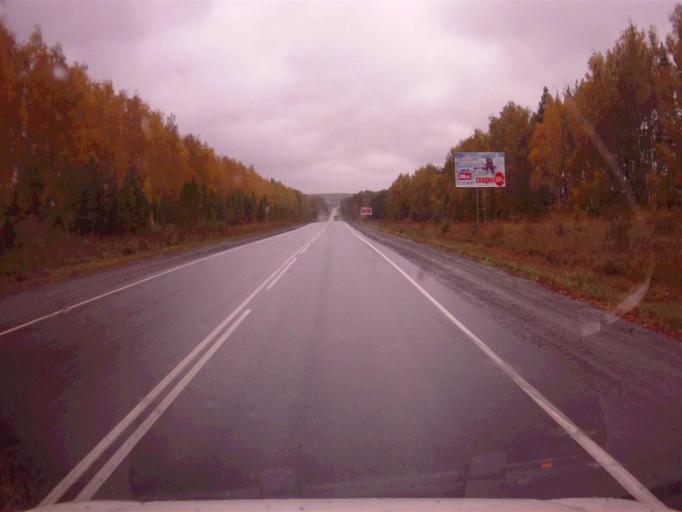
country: RU
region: Chelyabinsk
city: Roshchino
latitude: 55.3620
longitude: 61.2148
